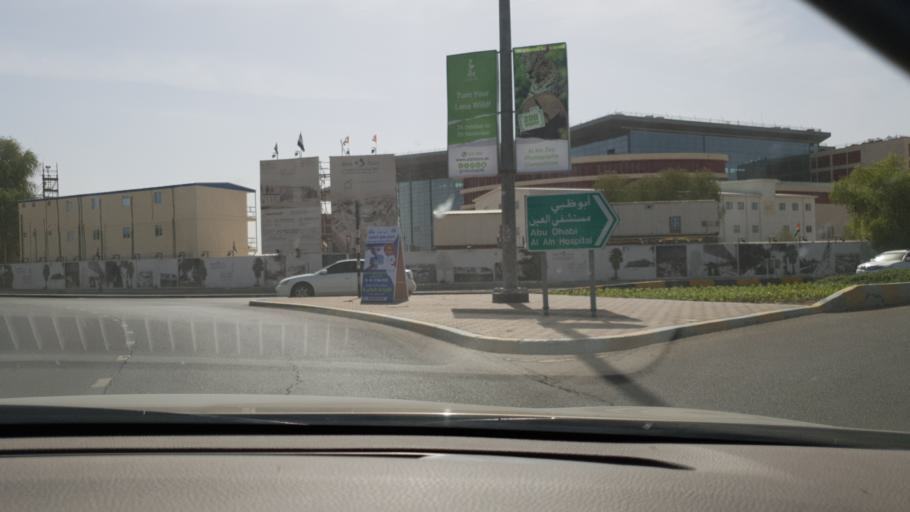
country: AE
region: Abu Dhabi
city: Al Ain
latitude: 24.2318
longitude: 55.7380
